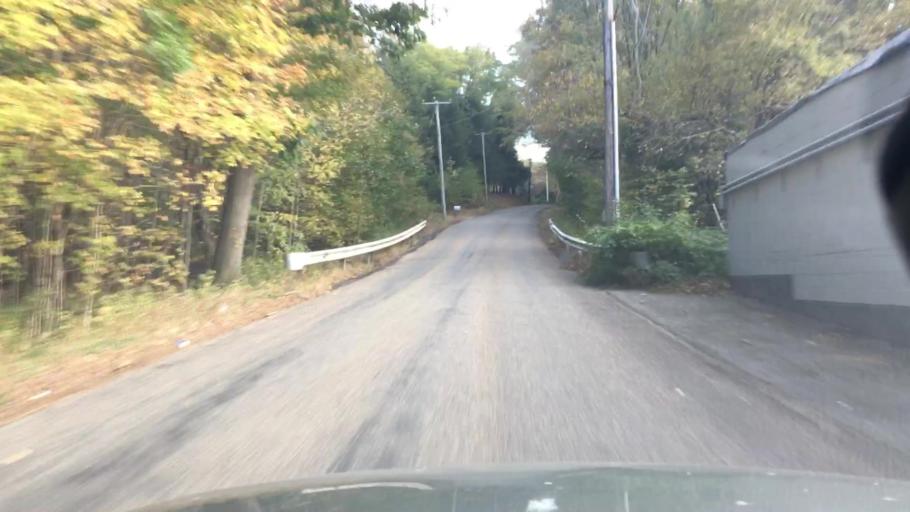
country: US
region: Connecticut
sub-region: Tolland County
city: Stafford
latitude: 41.9685
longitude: -72.2871
